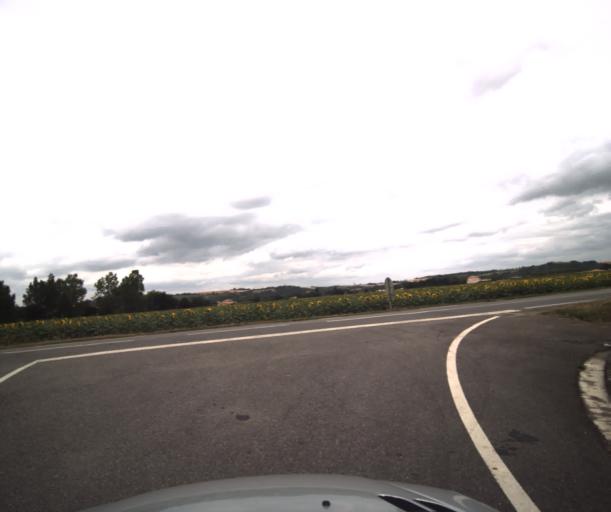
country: FR
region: Midi-Pyrenees
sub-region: Departement de la Haute-Garonne
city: Labarthe-sur-Leze
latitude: 43.4505
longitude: 1.4075
